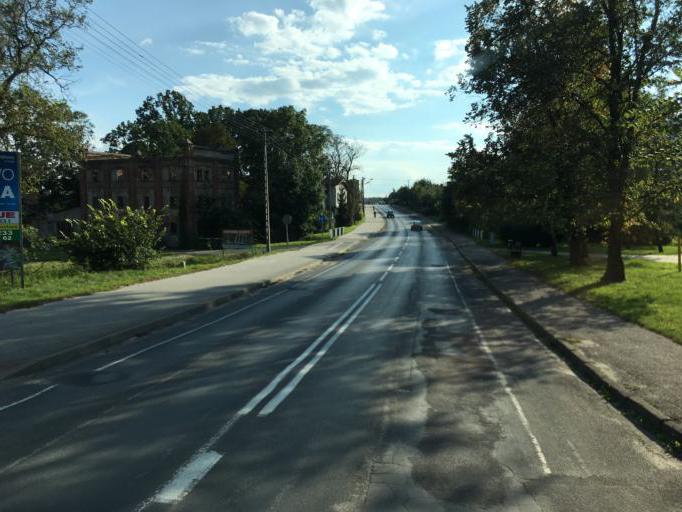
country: PL
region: Kujawsko-Pomorskie
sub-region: Powiat tucholski
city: Tuchola
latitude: 53.5790
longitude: 17.8681
